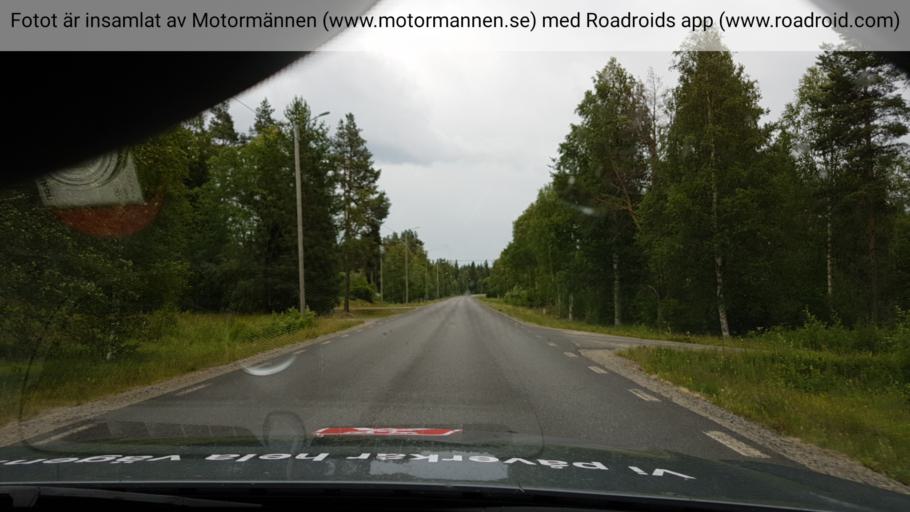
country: SE
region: Jaemtland
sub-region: Braecke Kommun
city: Braecke
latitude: 62.4279
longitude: 14.9946
